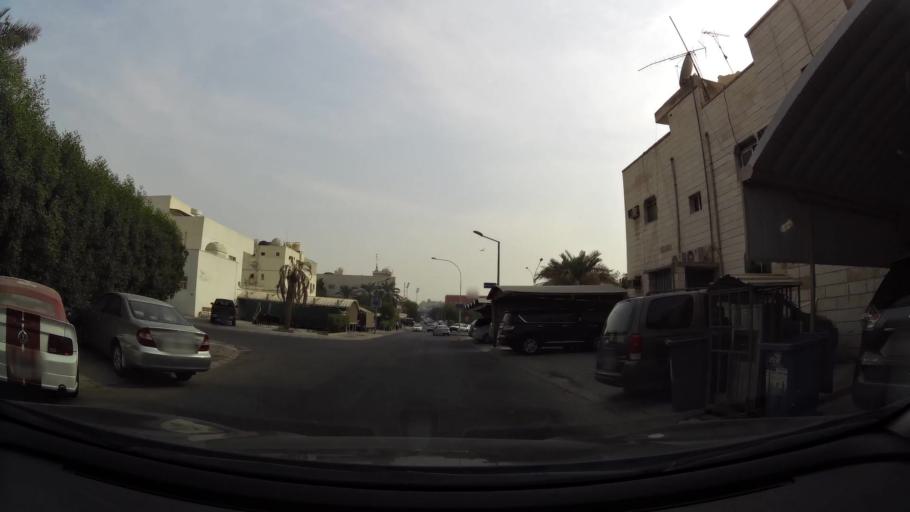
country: KW
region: Al Farwaniyah
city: Al Farwaniyah
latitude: 29.2950
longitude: 47.9623
